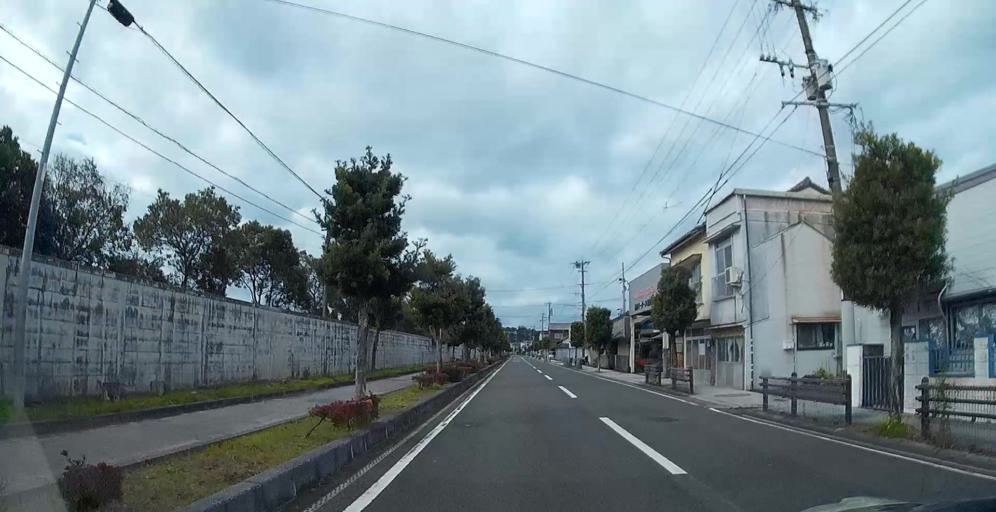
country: JP
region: Kumamoto
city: Minamata
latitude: 32.2111
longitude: 130.3933
